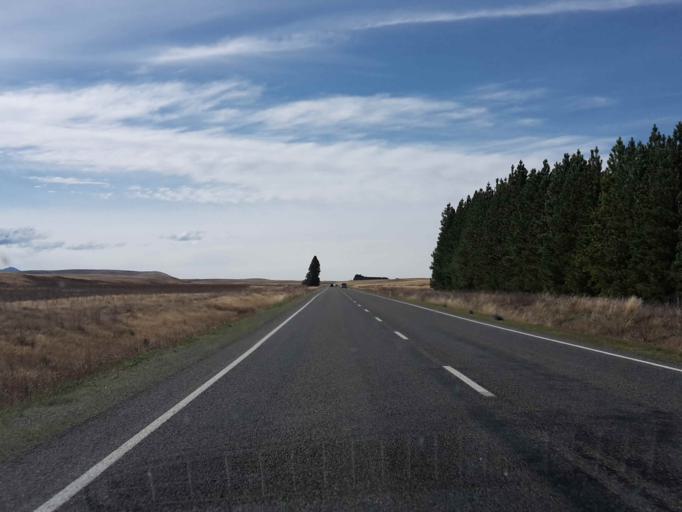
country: NZ
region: Canterbury
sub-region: Timaru District
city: Pleasant Point
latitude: -44.0545
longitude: 170.3716
